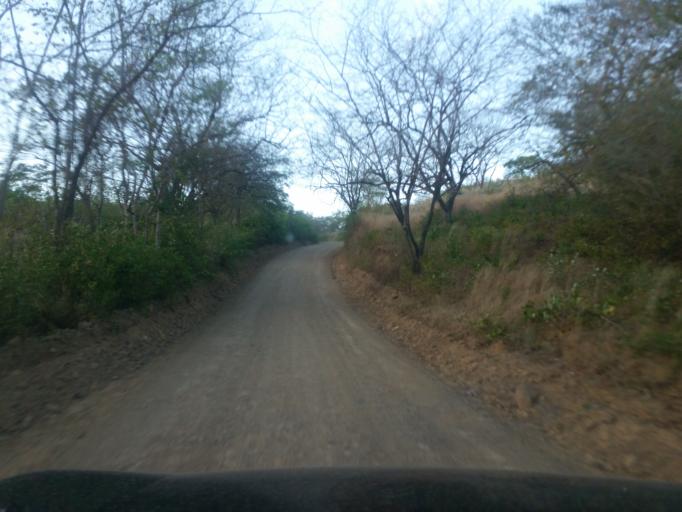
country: NI
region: Rivas
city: San Juan del Sur
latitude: 11.2117
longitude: -85.8088
